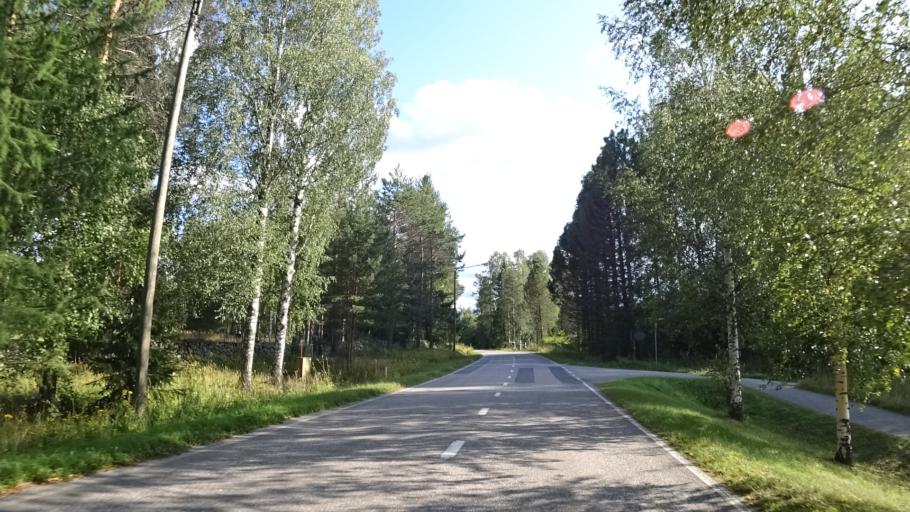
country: FI
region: North Karelia
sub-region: Keski-Karjala
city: Kesaelahti
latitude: 61.8868
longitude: 29.8383
